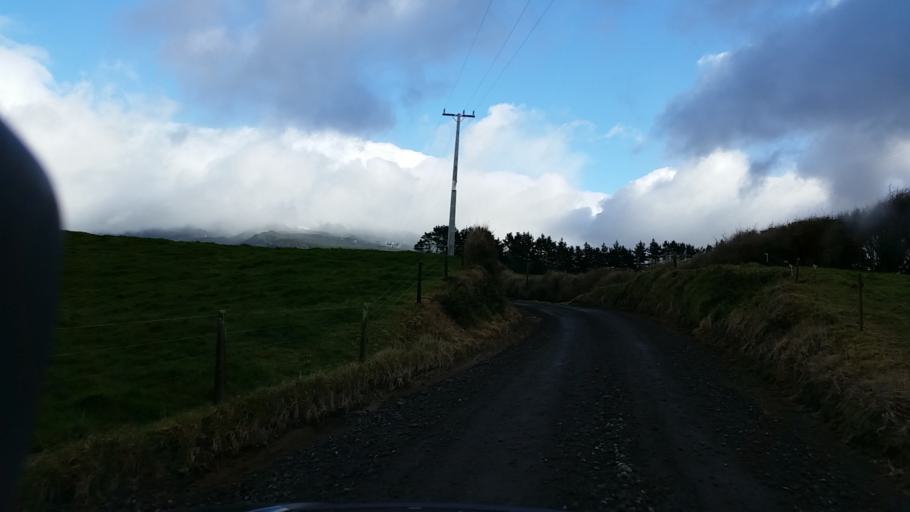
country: NZ
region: Taranaki
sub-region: South Taranaki District
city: Eltham
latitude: -39.3355
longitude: 174.1801
